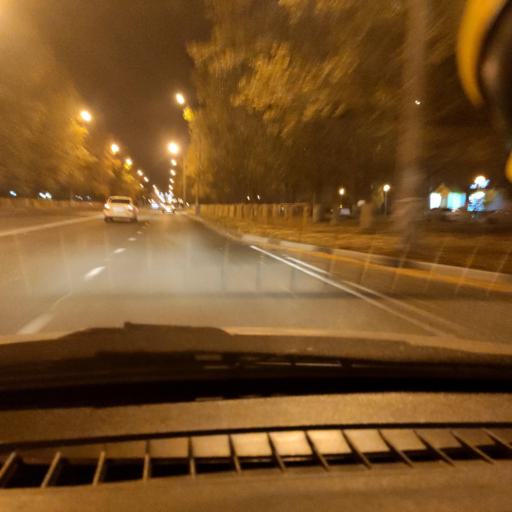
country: RU
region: Samara
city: Tol'yatti
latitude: 53.5374
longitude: 49.3446
